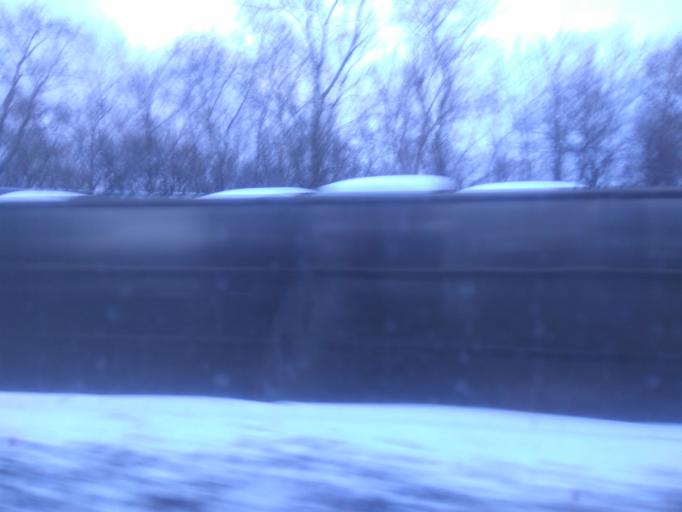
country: RU
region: Moscow
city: Taganskiy
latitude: 55.7307
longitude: 37.6947
